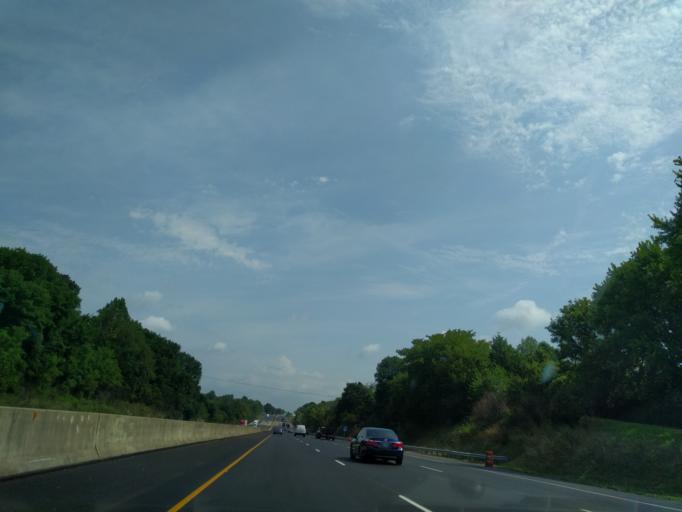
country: US
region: Kentucky
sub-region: Warren County
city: Bowling Green
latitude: 36.9838
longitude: -86.3877
